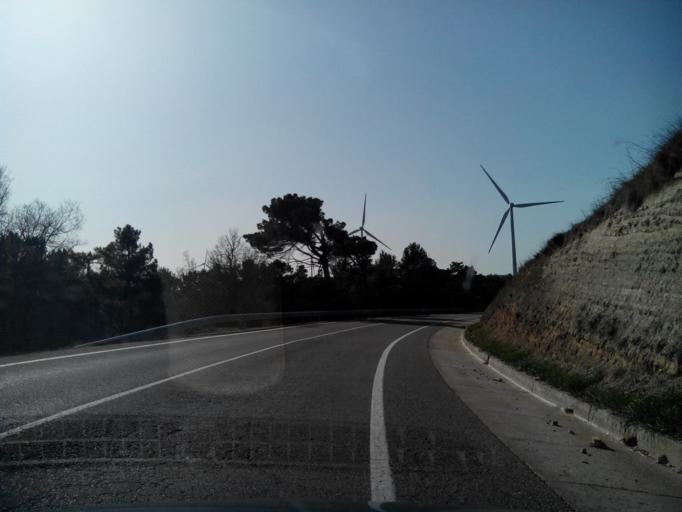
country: ES
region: Catalonia
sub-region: Provincia de Tarragona
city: Santa Coloma de Queralt
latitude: 41.5815
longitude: 1.3922
